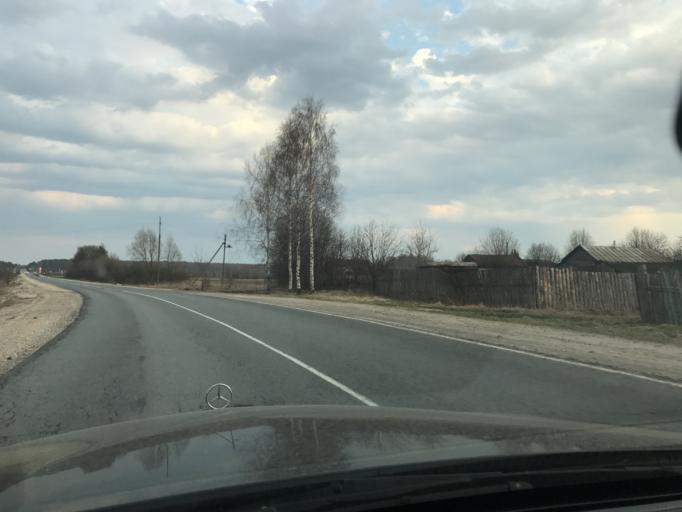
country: RU
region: Vladimir
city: Murom
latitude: 55.6265
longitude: 41.8874
